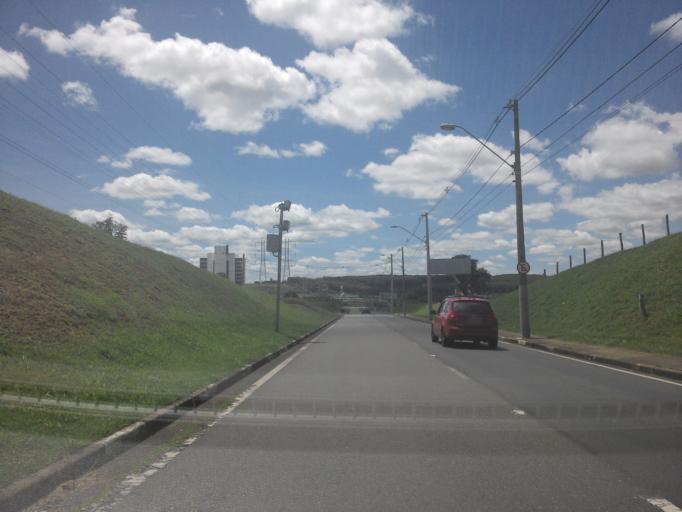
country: BR
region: Sao Paulo
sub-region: Campinas
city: Campinas
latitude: -22.8927
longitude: -47.0221
